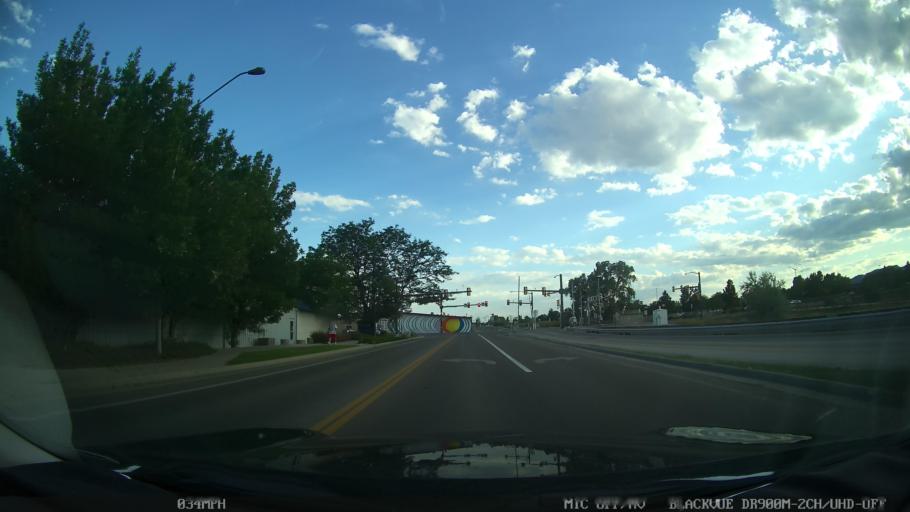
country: US
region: Colorado
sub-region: Larimer County
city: Fort Collins
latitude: 40.5392
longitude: -105.0804
